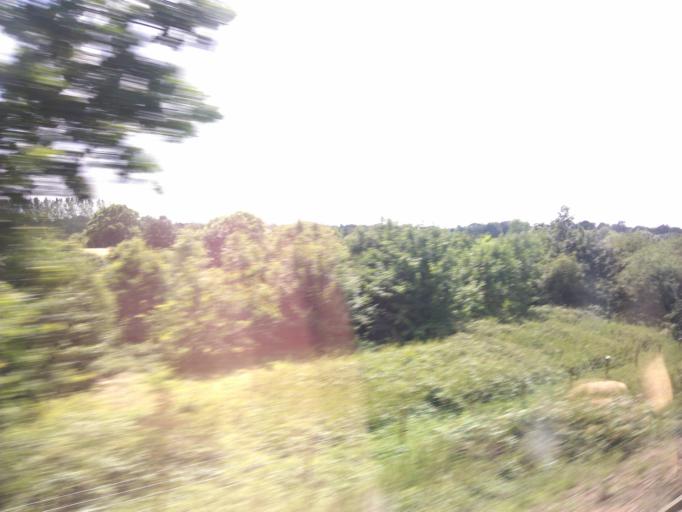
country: GB
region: England
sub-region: Essex
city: Eight Ash Green
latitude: 51.8881
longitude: 0.8114
